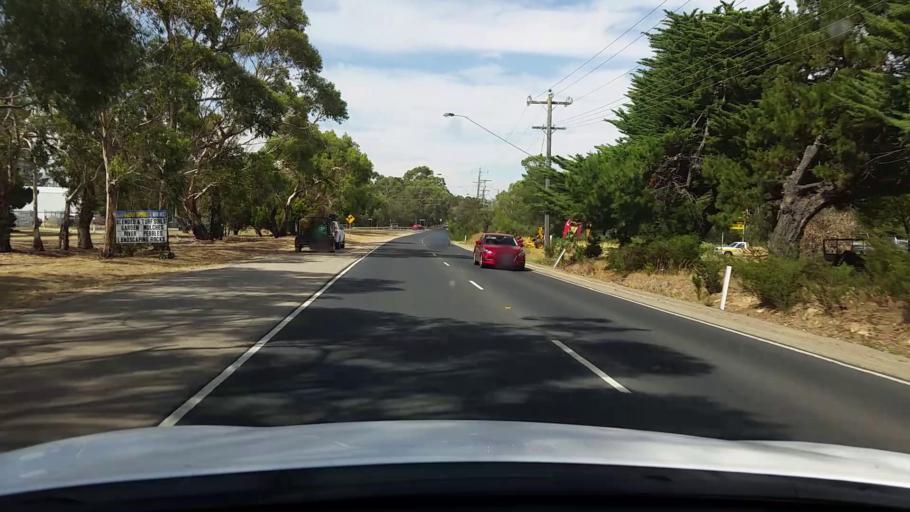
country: AU
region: Victoria
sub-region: Mornington Peninsula
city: Hastings
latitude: -38.3148
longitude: 145.1836
